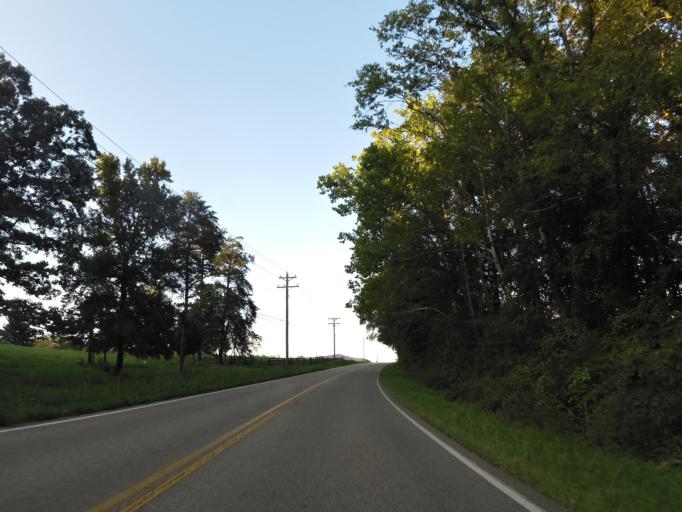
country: US
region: Tennessee
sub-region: Roane County
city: Rockwood
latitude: 35.7281
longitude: -84.6324
